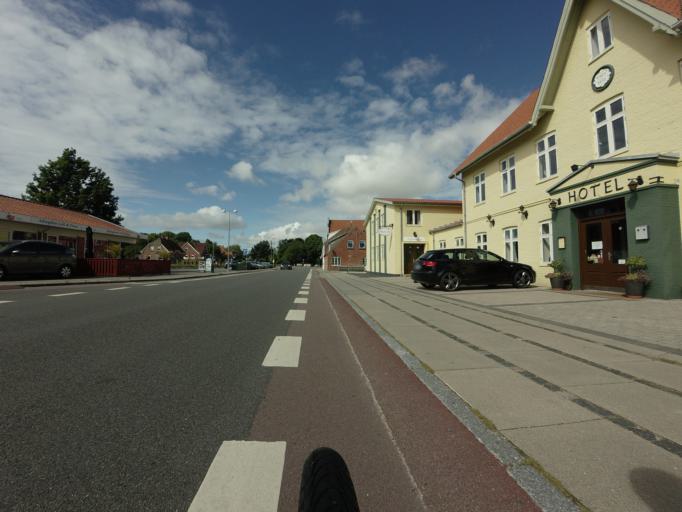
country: DK
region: Central Jutland
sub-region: Norddjurs Kommune
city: Allingabro
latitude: 56.4642
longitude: 10.3201
